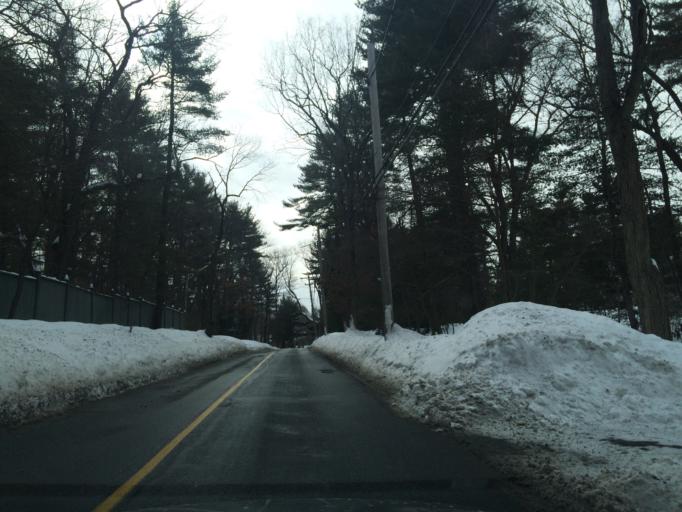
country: US
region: Massachusetts
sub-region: Middlesex County
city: Weston
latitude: 42.3488
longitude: -71.2821
